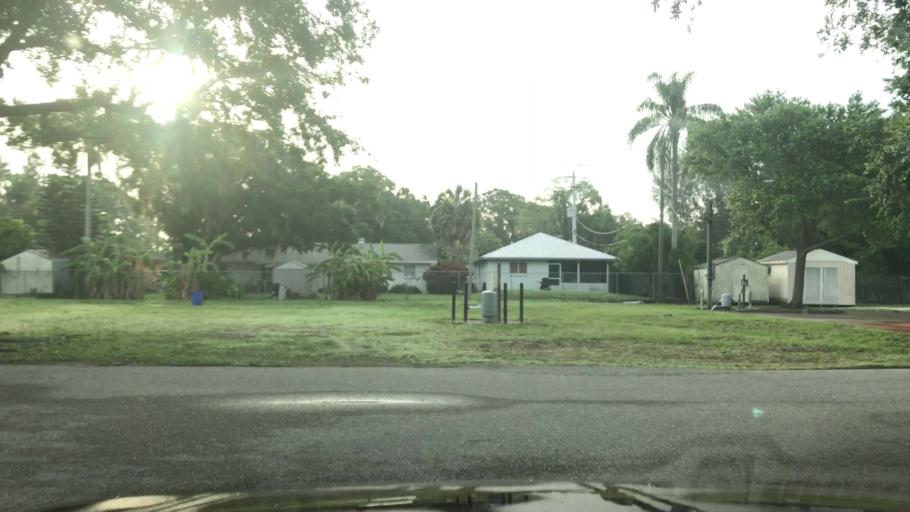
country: US
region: Florida
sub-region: Sarasota County
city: Fruitville
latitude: 27.3245
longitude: -82.4604
